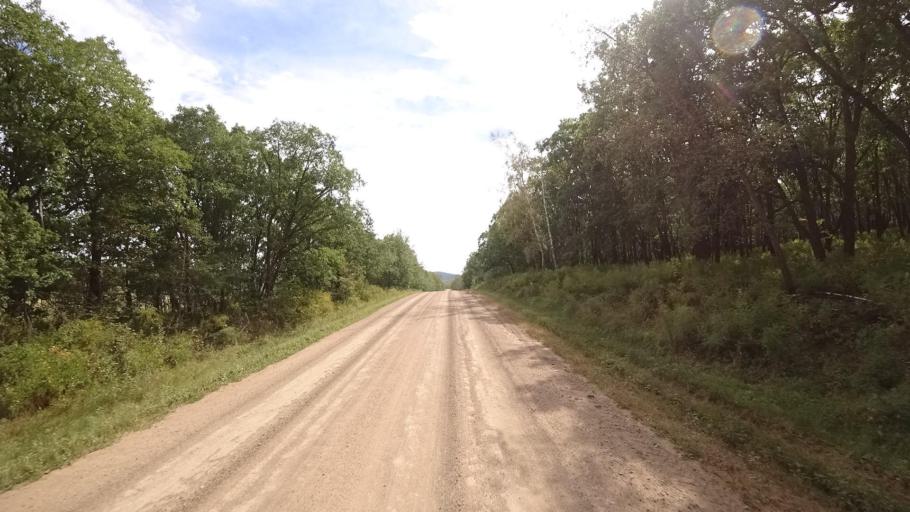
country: RU
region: Primorskiy
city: Yakovlevka
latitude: 44.6052
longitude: 133.6025
